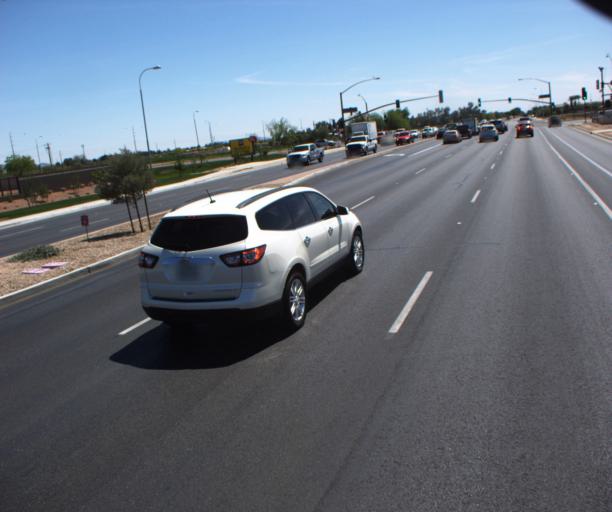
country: US
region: Arizona
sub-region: Maricopa County
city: Chandler
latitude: 33.2633
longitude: -111.8415
